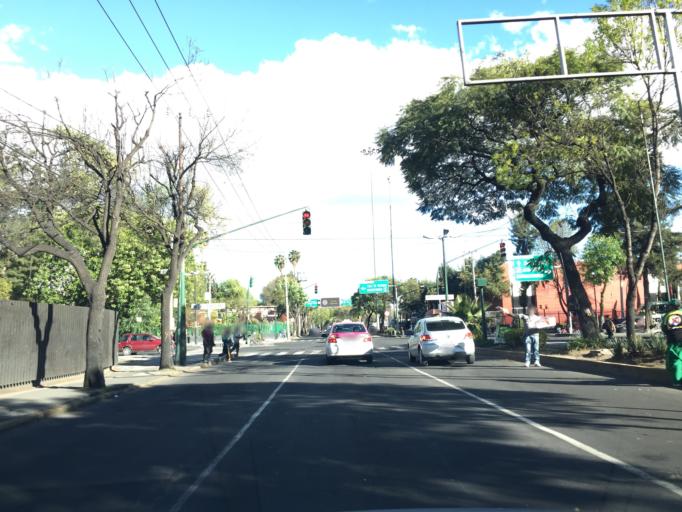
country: MX
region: Mexico
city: Colonia Lindavista
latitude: 19.4851
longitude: -99.1352
